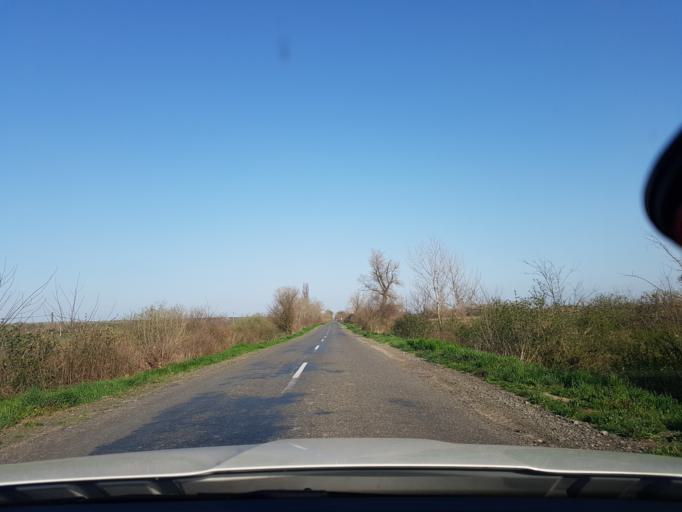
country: HU
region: Tolna
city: Ocseny
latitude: 46.3393
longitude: 18.7694
